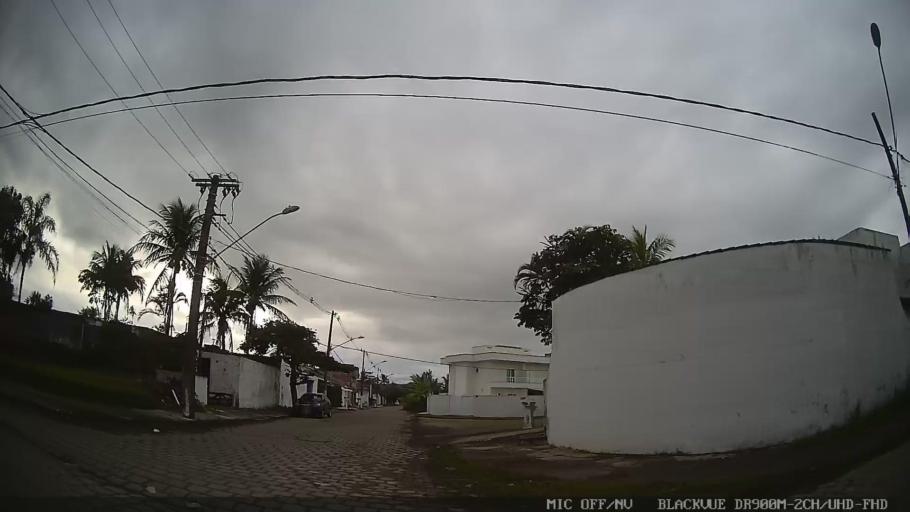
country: BR
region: Sao Paulo
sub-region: Itanhaem
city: Itanhaem
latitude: -24.2009
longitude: -46.8196
